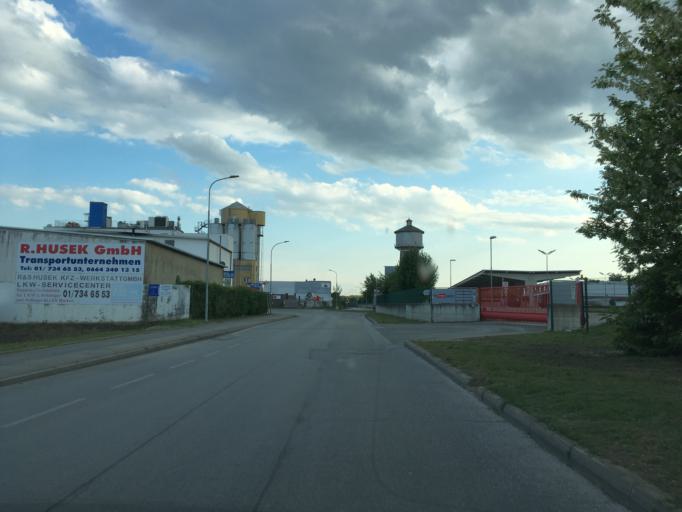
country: AT
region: Lower Austria
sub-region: Politischer Bezirk Wien-Umgebung
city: Gerasdorf bei Wien
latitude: 48.2801
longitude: 16.4788
